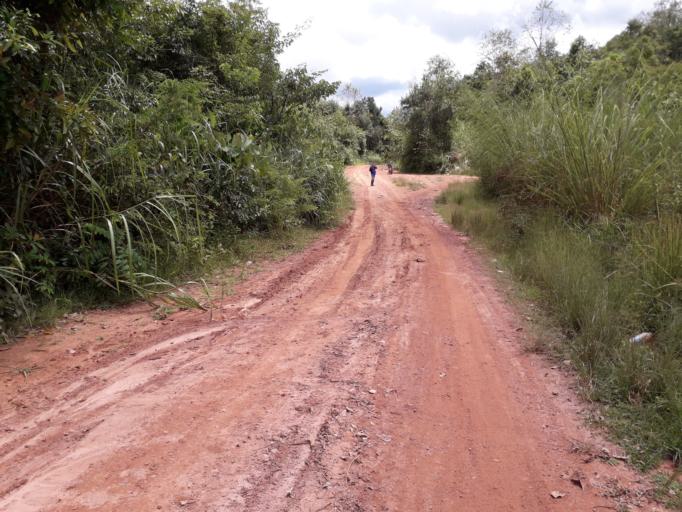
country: CN
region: Yunnan
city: Menglie
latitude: 22.2702
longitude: 101.5671
